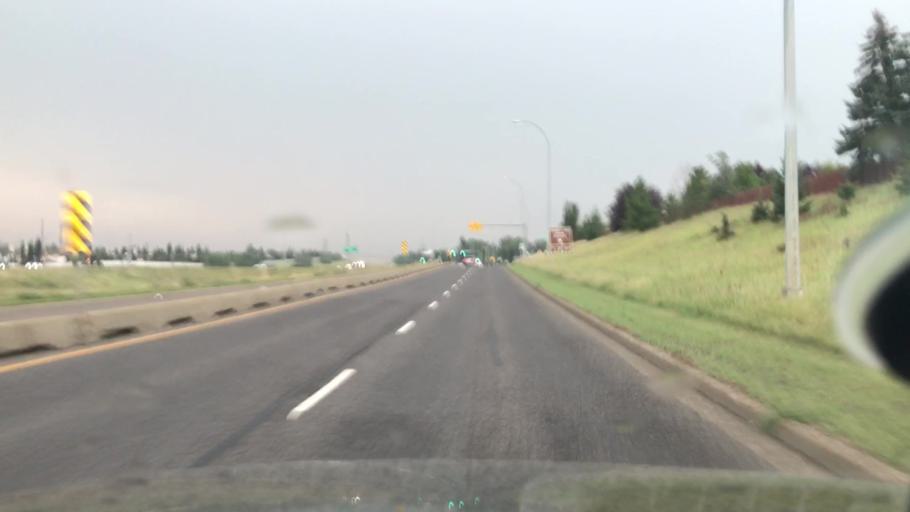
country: CA
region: Alberta
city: Edmonton
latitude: 53.4708
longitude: -113.5802
